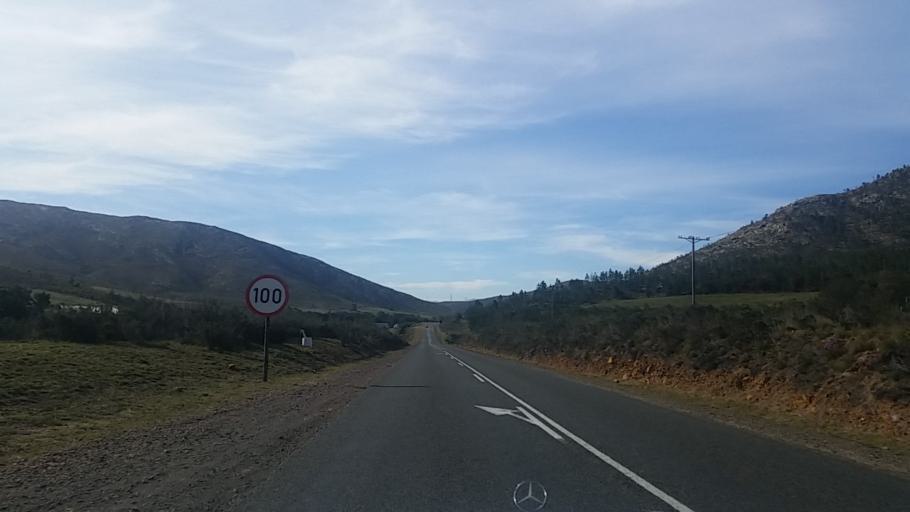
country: ZA
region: Western Cape
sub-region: Eden District Municipality
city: George
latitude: -33.8407
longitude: 22.3497
